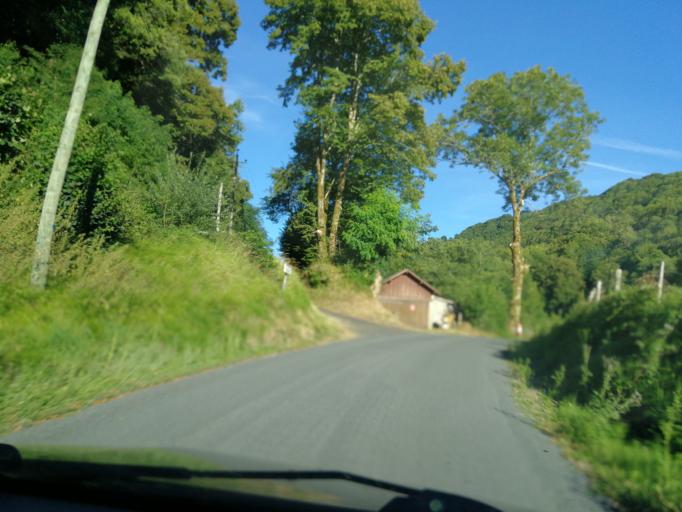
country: FR
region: Auvergne
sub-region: Departement du Cantal
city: Saint-Cernin
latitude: 45.1010
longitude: 2.5363
